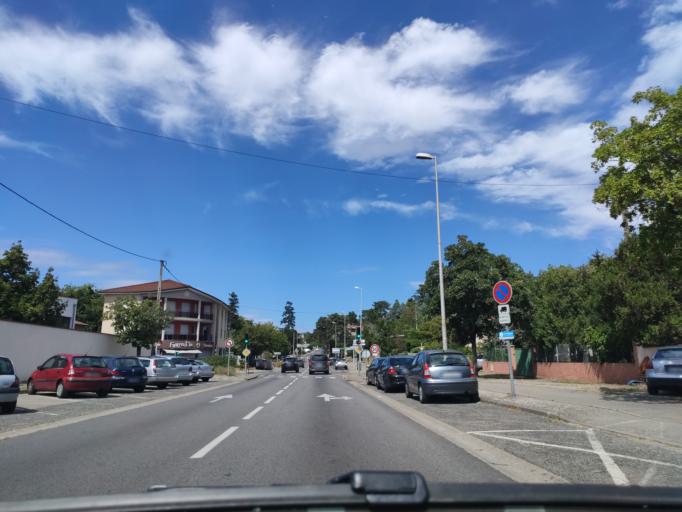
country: FR
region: Rhone-Alpes
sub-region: Departement de l'Isere
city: Le Peage-de-Roussillon
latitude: 45.3707
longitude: 4.8012
